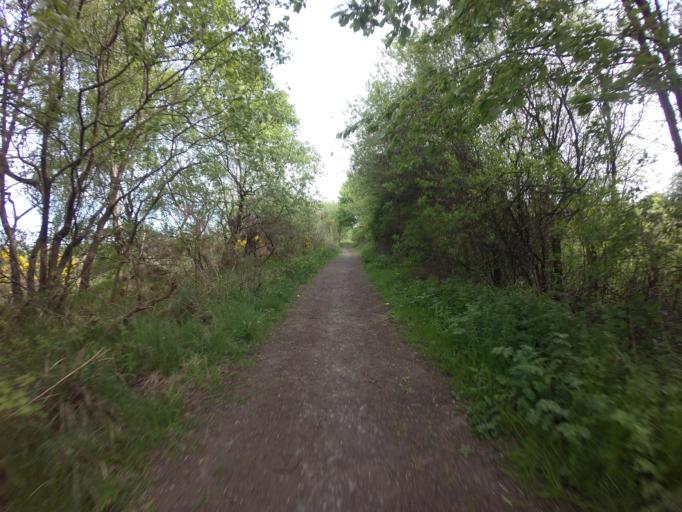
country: GB
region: Scotland
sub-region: West Lothian
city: Mid Calder
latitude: 55.9168
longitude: -3.4935
